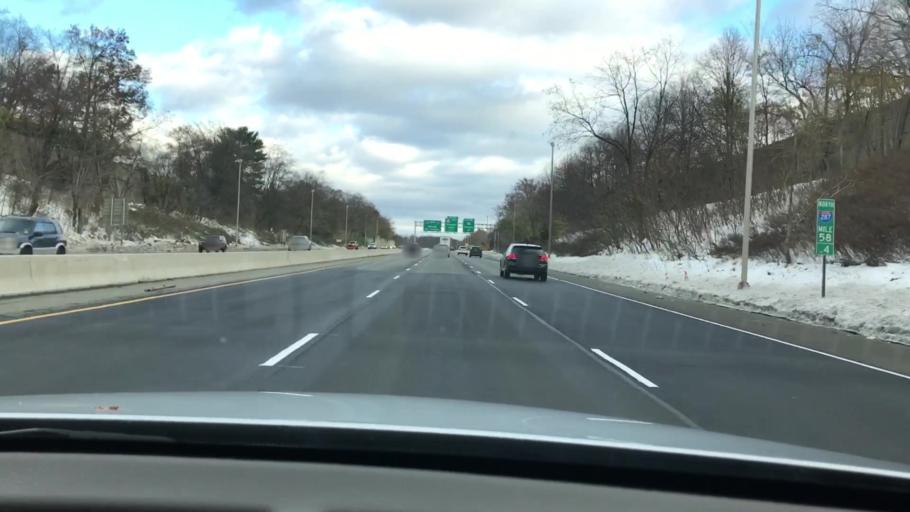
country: US
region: New Jersey
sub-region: Bergen County
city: Oakland
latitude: 41.0286
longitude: -74.2468
